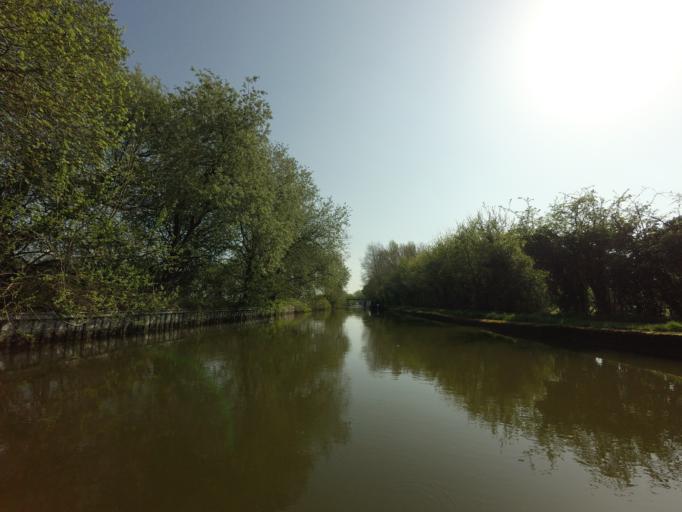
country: GB
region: England
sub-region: Buckinghamshire
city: Aston Clinton
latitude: 51.8204
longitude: -0.6932
